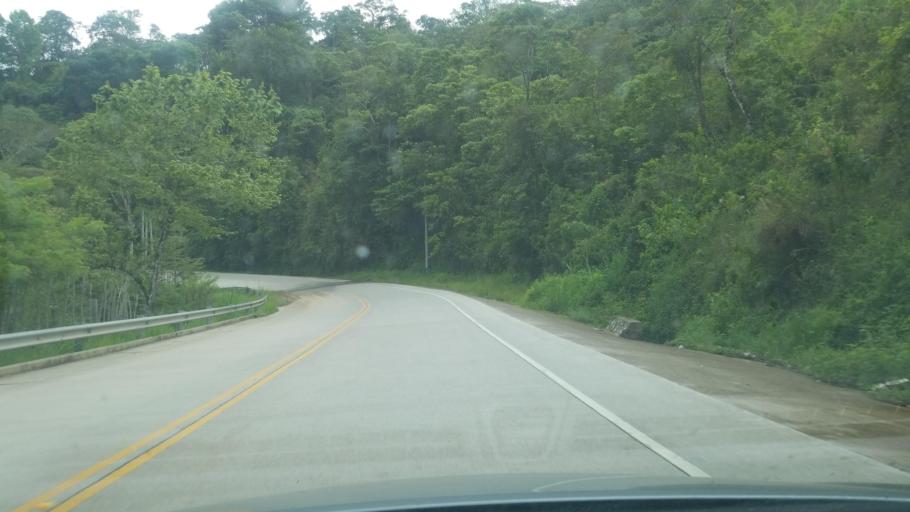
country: HN
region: Copan
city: San Jeronimo
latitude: 14.9296
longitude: -88.9384
